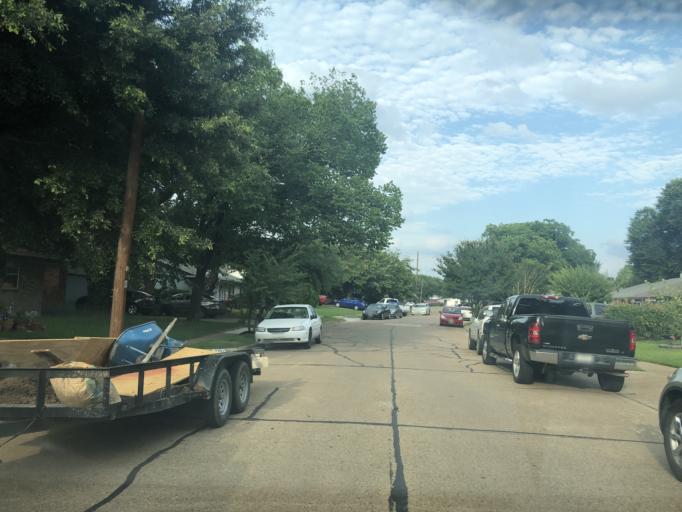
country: US
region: Texas
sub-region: Dallas County
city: Irving
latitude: 32.7891
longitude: -96.9767
